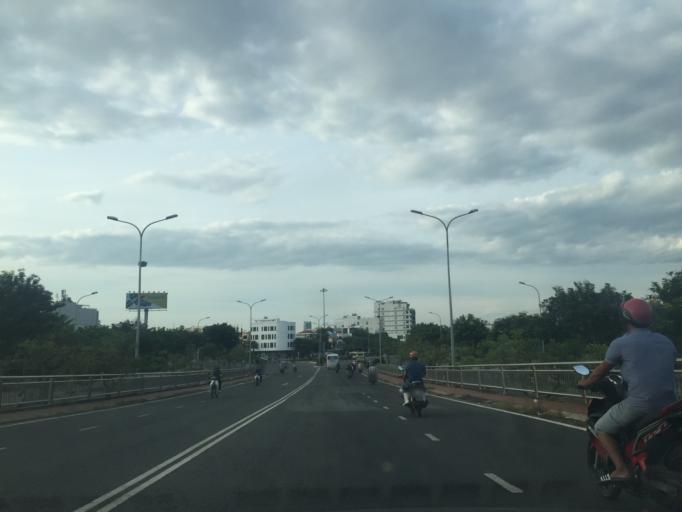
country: VN
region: Da Nang
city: Da Nang
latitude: 16.0897
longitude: 108.2150
